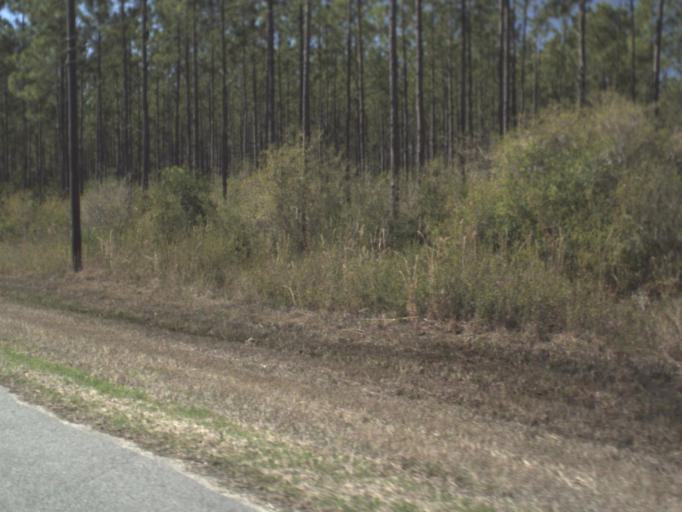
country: US
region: Florida
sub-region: Bay County
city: Laguna Beach
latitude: 30.3015
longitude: -85.8289
